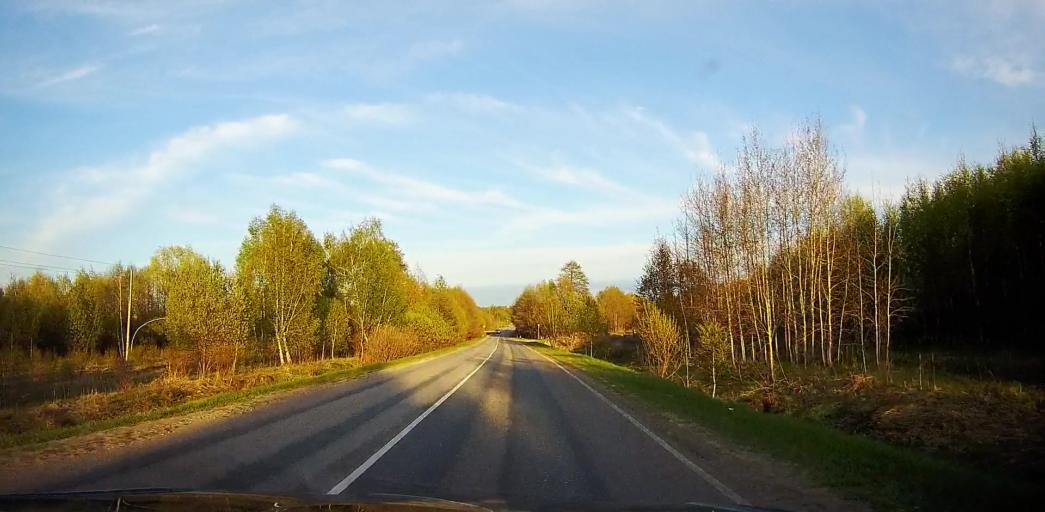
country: RU
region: Moskovskaya
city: Meshcherino
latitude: 55.2480
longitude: 38.2971
